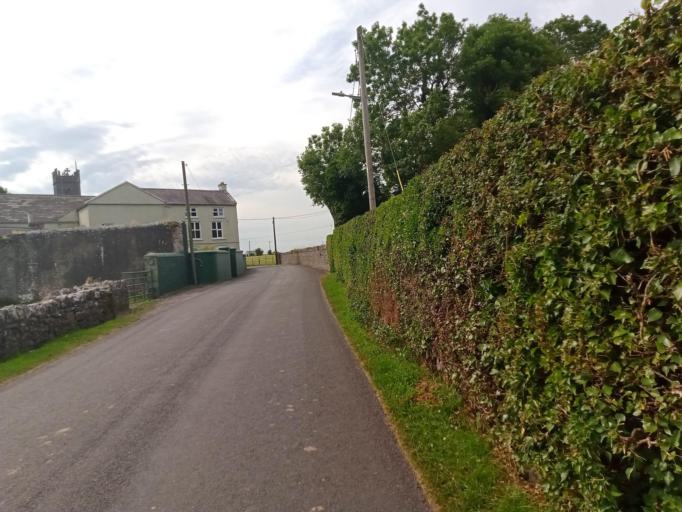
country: IE
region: Leinster
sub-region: Laois
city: Rathdowney
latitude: 52.8222
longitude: -7.4806
